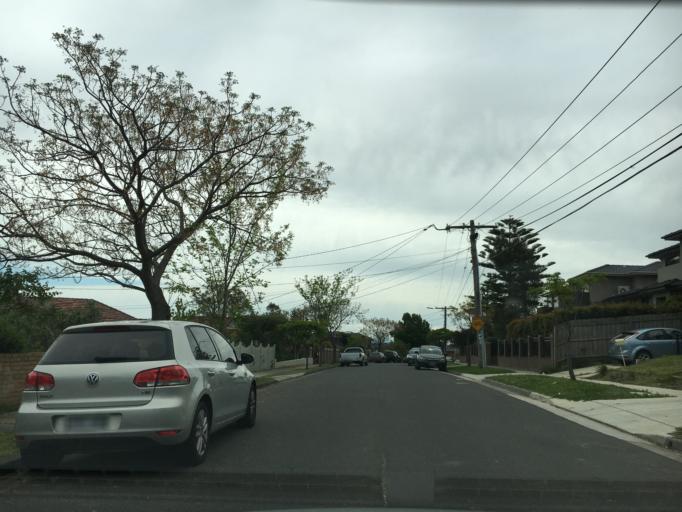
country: AU
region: Victoria
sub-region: Monash
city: Chadstone
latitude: -37.8899
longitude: 145.0964
